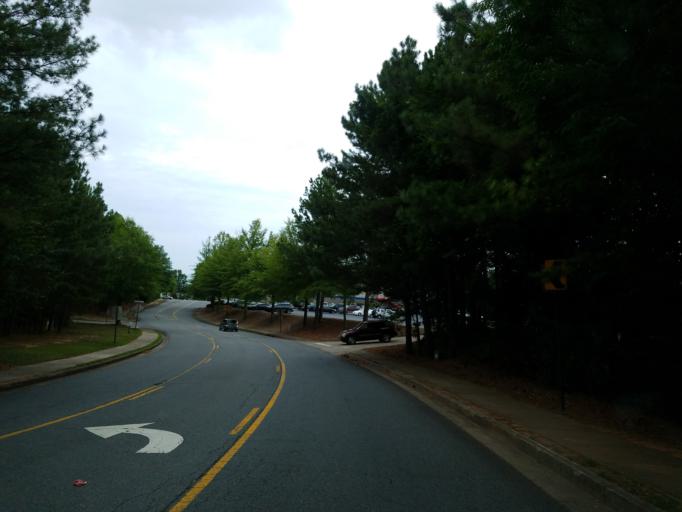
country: US
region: Georgia
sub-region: Cherokee County
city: Woodstock
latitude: 34.0401
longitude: -84.4661
